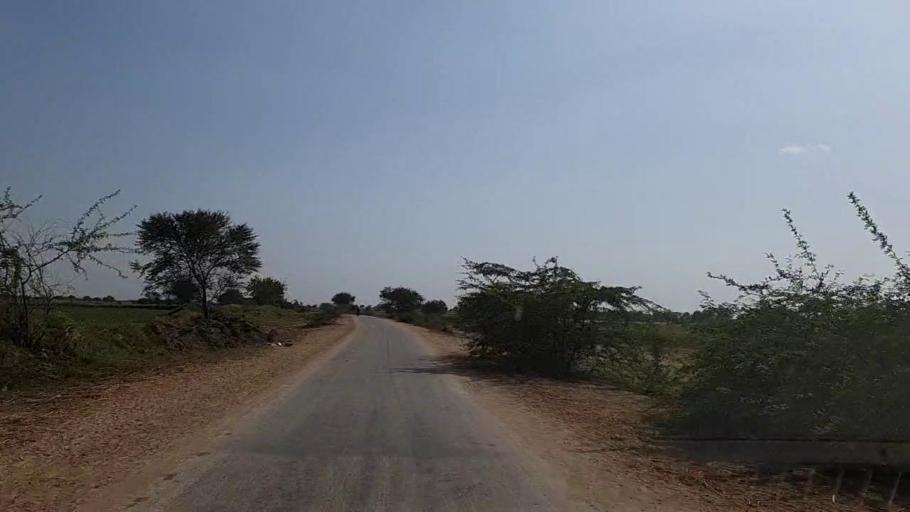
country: PK
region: Sindh
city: Daro Mehar
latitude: 24.7844
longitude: 68.1801
